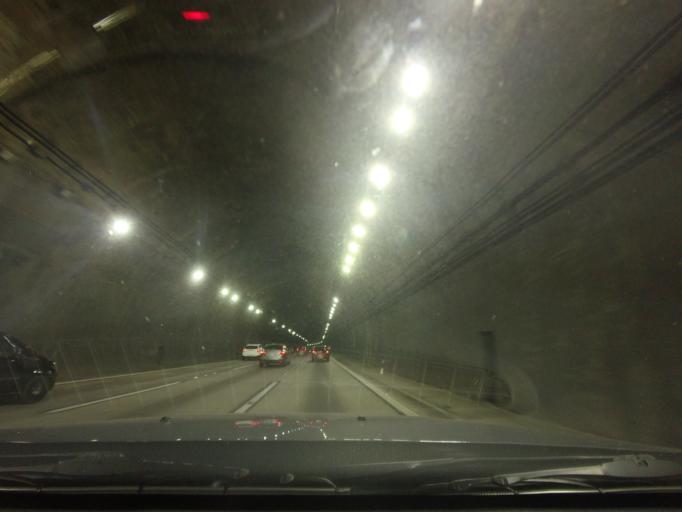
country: BR
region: Sao Paulo
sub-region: Cubatao
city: Cubatao
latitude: -23.8931
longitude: -46.4944
